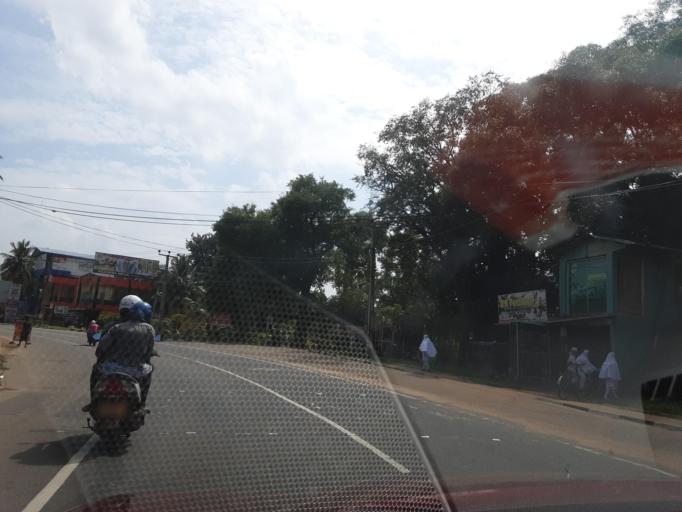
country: LK
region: Northern Province
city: Vavuniya
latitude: 8.5363
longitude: 80.4941
